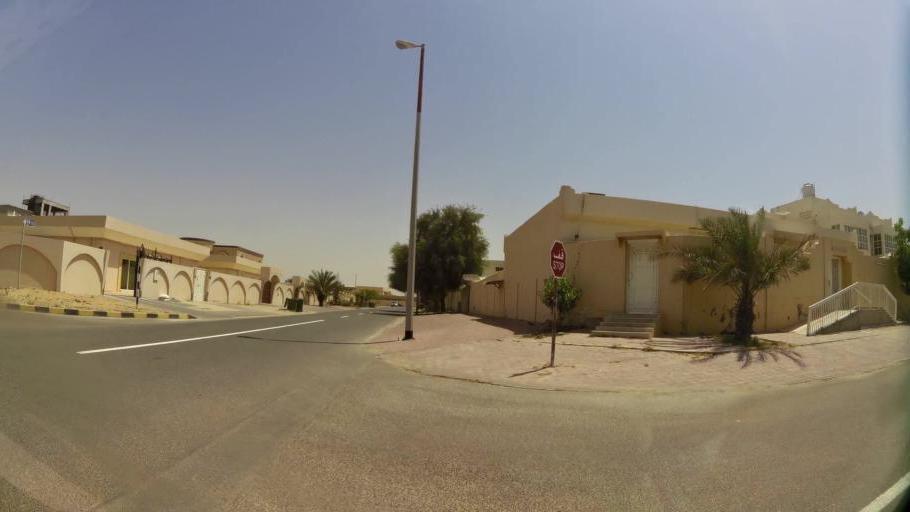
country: AE
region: Ajman
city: Ajman
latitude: 25.4247
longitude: 55.5047
